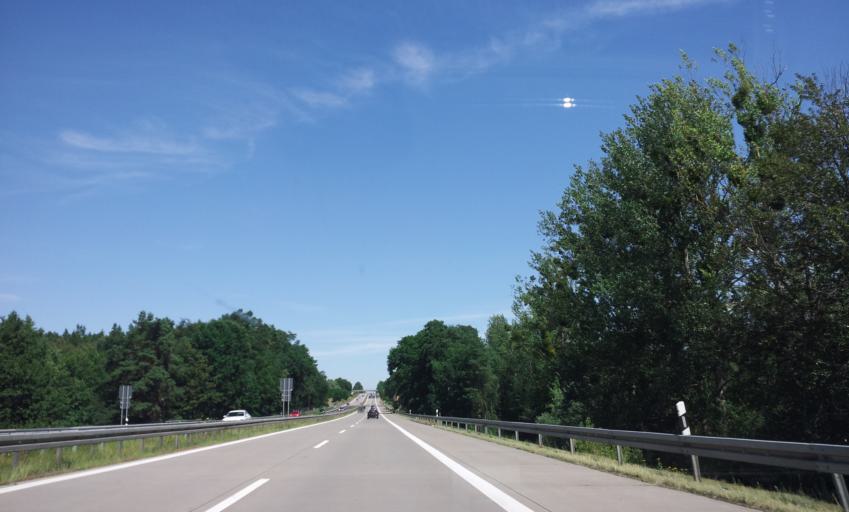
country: DE
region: Brandenburg
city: Althuttendorf
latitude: 53.0677
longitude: 13.8424
